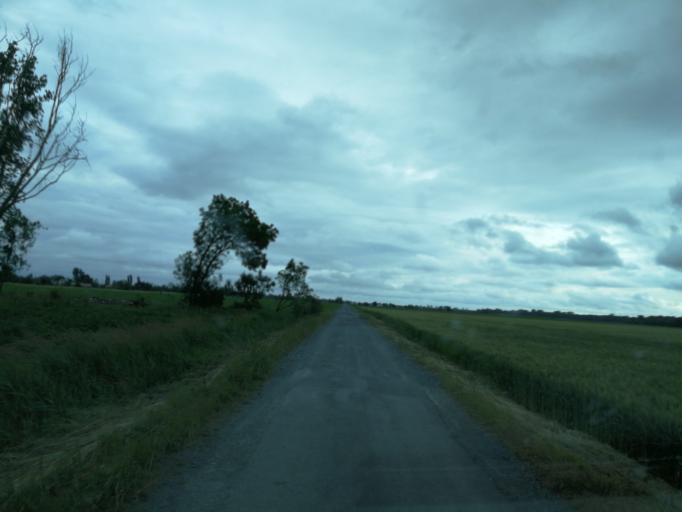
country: FR
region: Pays de la Loire
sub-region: Departement de la Vendee
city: Vix
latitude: 46.3656
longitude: -0.9342
